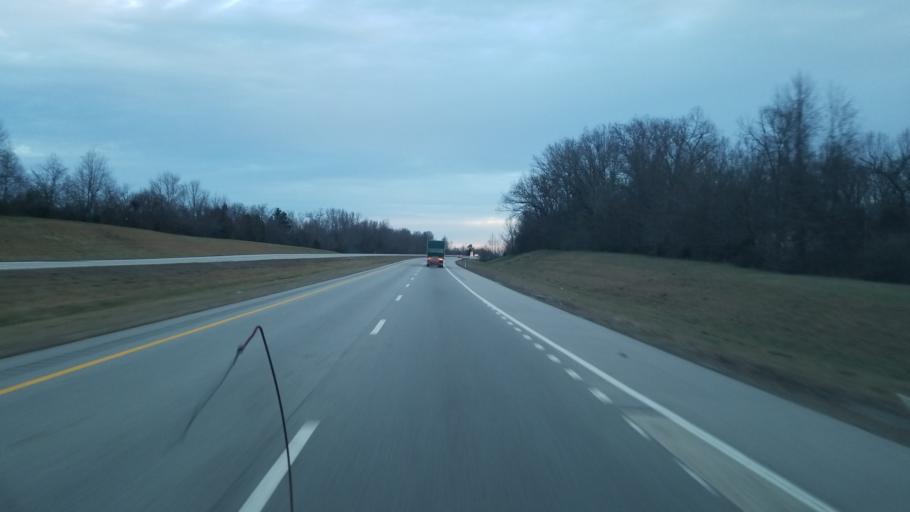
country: US
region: Tennessee
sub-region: White County
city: Sparta
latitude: 36.0246
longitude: -85.5086
